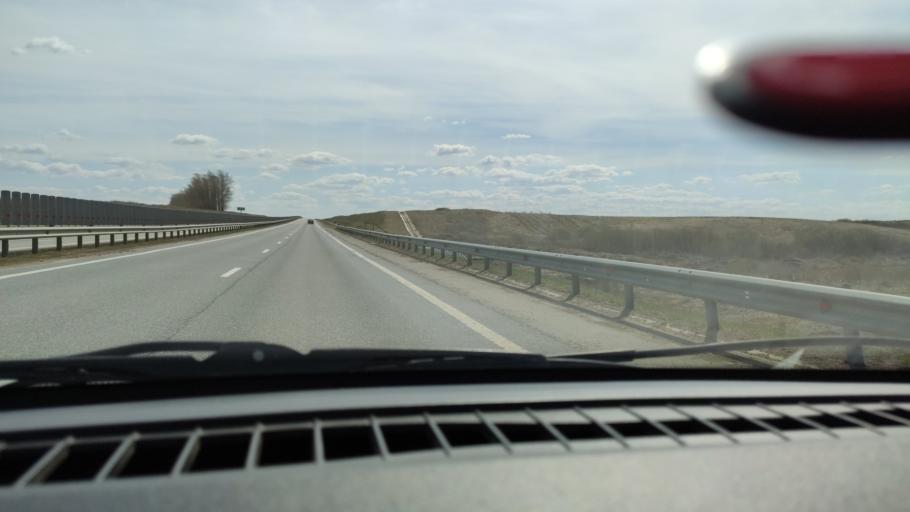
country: RU
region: Bashkortostan
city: Kushnarenkovo
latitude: 55.0999
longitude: 55.2409
